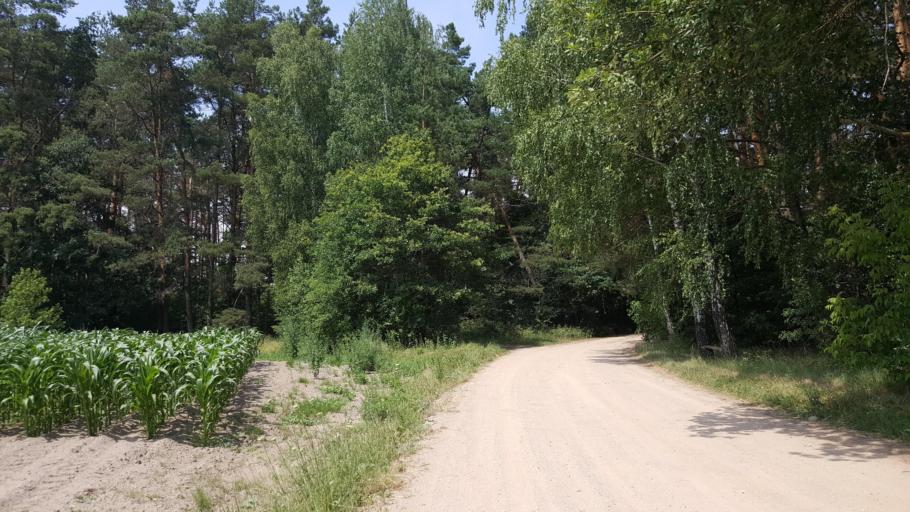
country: BY
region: Brest
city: Kamyanyets
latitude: 52.3833
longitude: 23.7830
